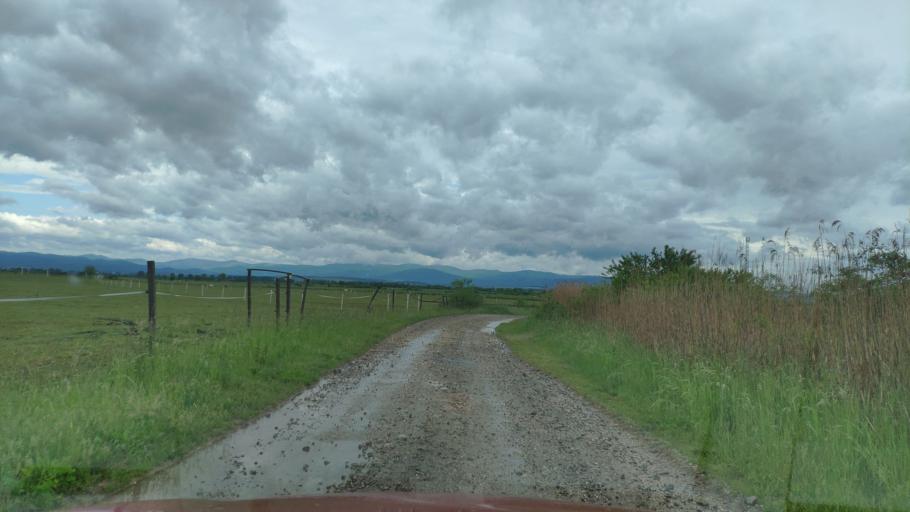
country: SK
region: Kosicky
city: Moldava nad Bodvou
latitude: 48.5417
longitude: 21.1125
